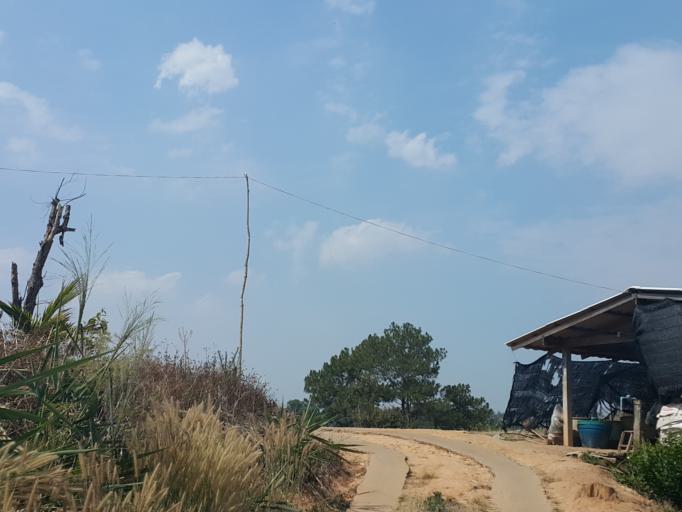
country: TH
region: Chiang Mai
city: Samoeng
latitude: 18.8852
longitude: 98.7946
